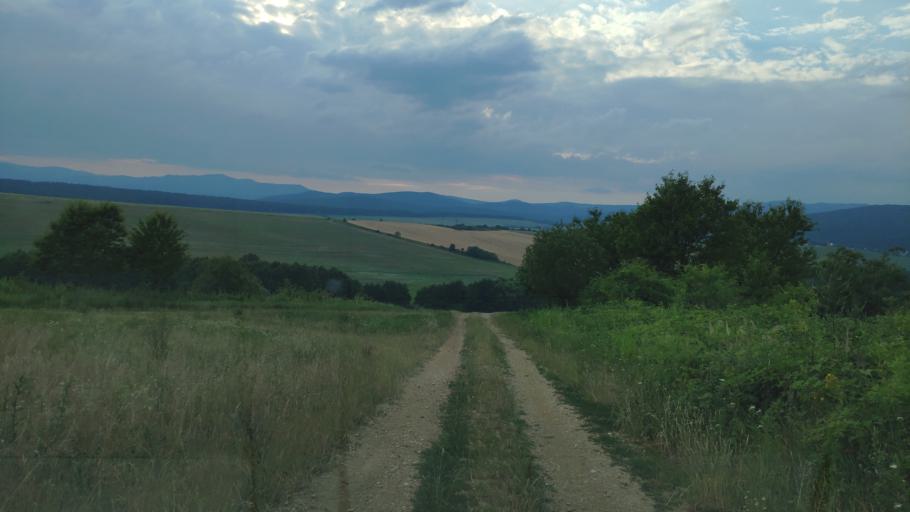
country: SK
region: Kosicky
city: Moldava nad Bodvou
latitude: 48.6975
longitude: 20.9898
